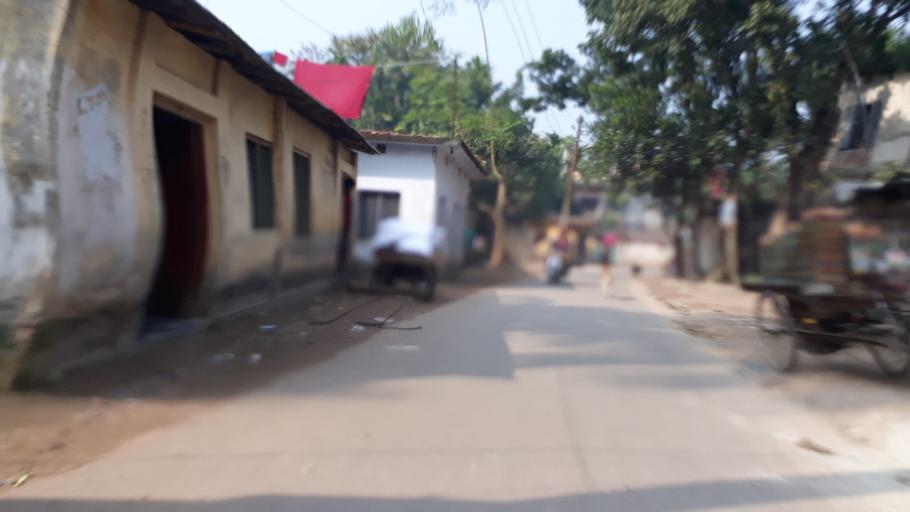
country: BD
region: Khulna
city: Kaliganj
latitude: 23.3550
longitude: 88.9146
